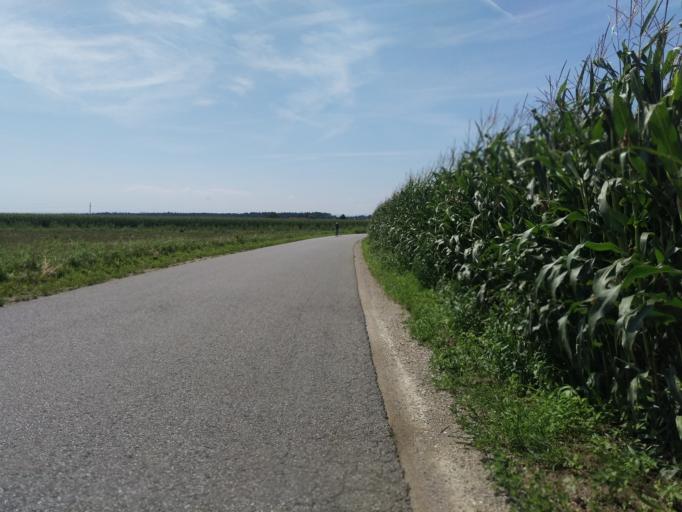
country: AT
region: Styria
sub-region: Politischer Bezirk Graz-Umgebung
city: Unterpremstatten
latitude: 46.9813
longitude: 15.4108
